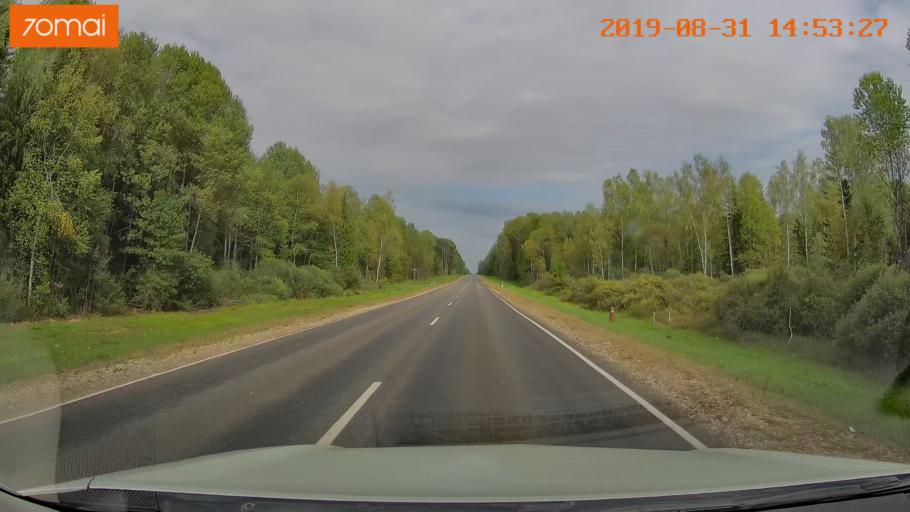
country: RU
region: Kaluga
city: Spas-Demensk
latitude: 54.2834
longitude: 33.8648
